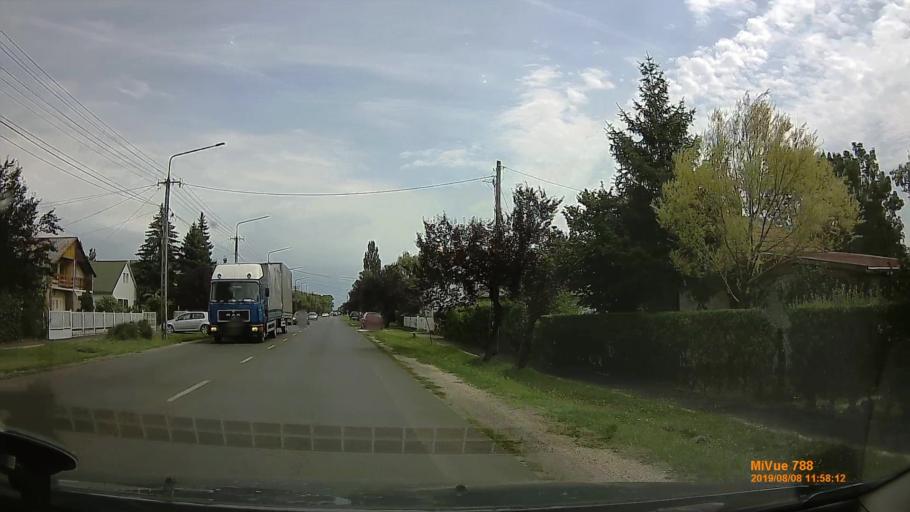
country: HU
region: Somogy
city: Balatonlelle
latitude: 46.7900
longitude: 17.7067
